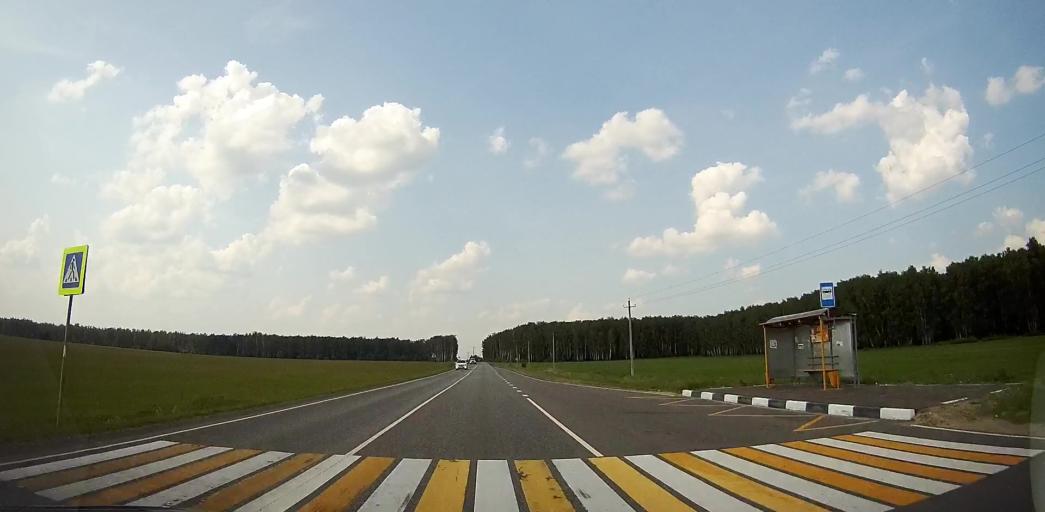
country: RU
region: Moskovskaya
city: Malino
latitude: 55.0492
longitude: 38.1467
